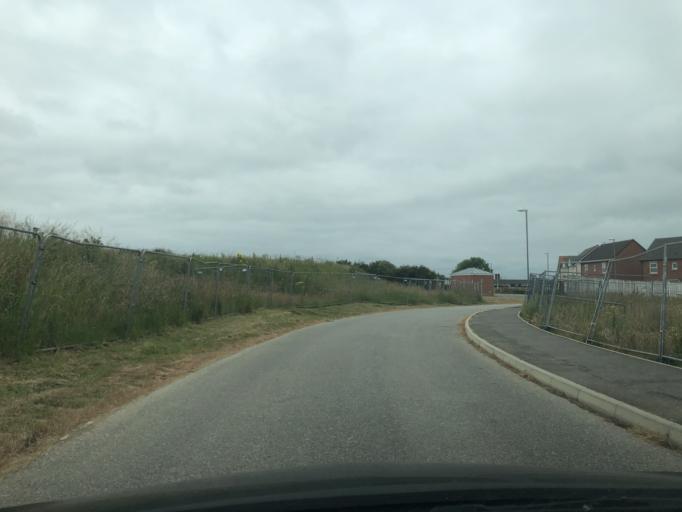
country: GB
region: England
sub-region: North Yorkshire
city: Filey
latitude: 54.2032
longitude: -0.2999
